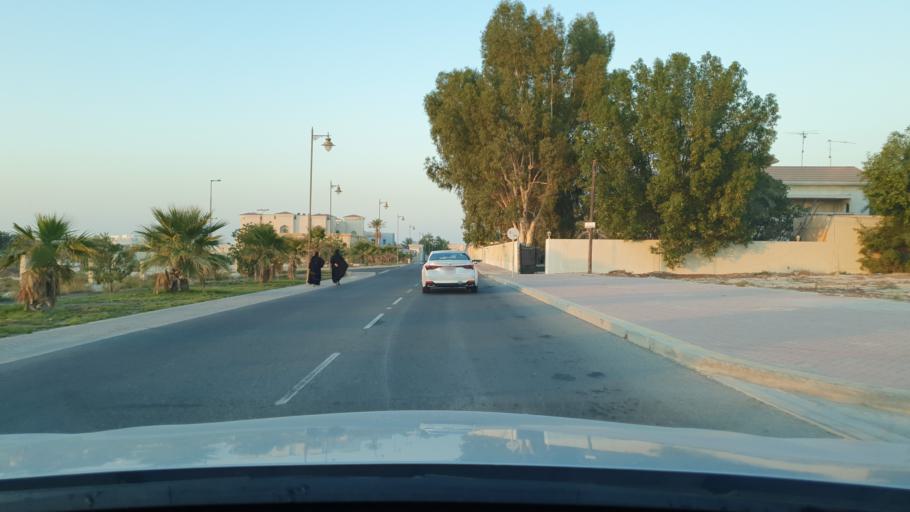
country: BH
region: Northern
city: Ar Rifa'
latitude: 26.1369
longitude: 50.5324
